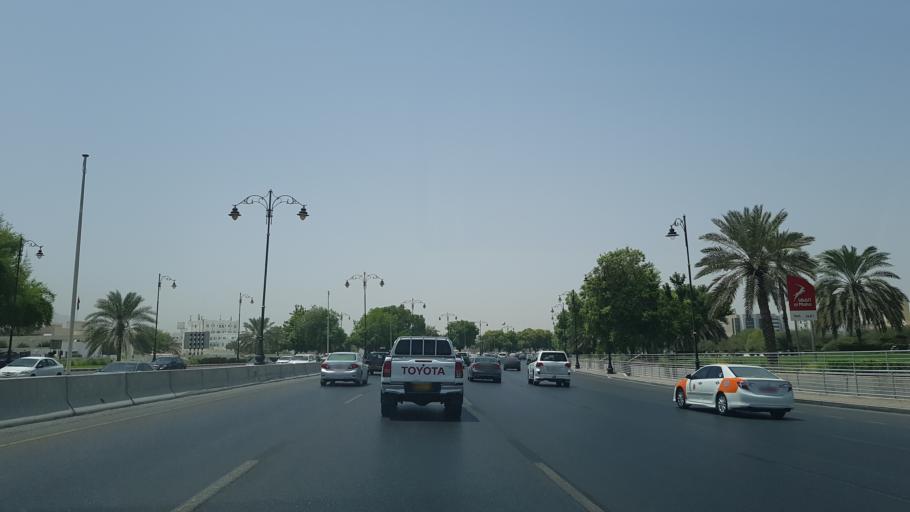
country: OM
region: Muhafazat Masqat
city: Bawshar
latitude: 23.5844
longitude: 58.4057
